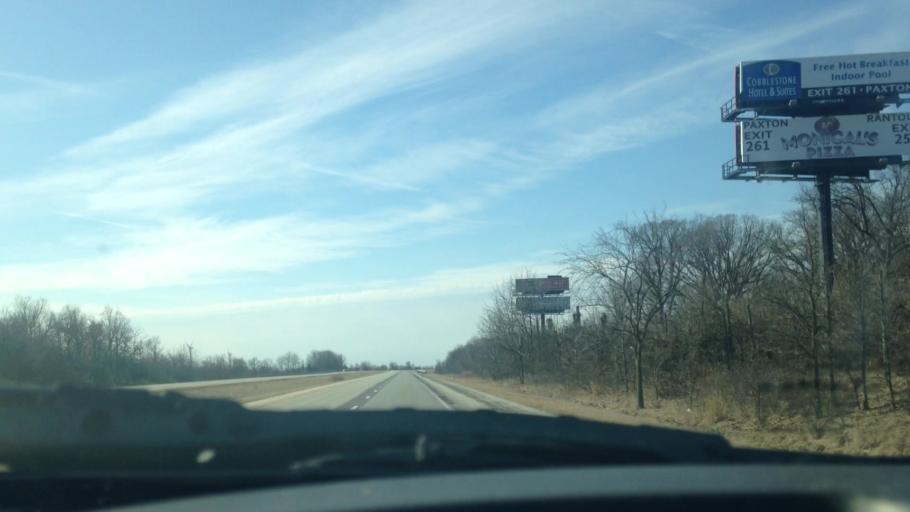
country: US
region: Illinois
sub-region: Ford County
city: Paxton
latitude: 40.5143
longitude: -88.0848
